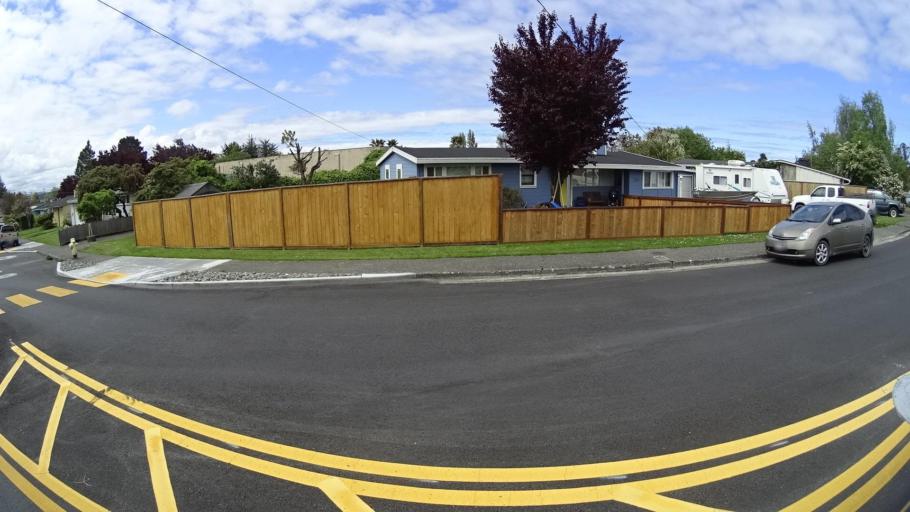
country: US
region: California
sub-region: Humboldt County
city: Arcata
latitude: 40.8584
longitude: -124.0706
